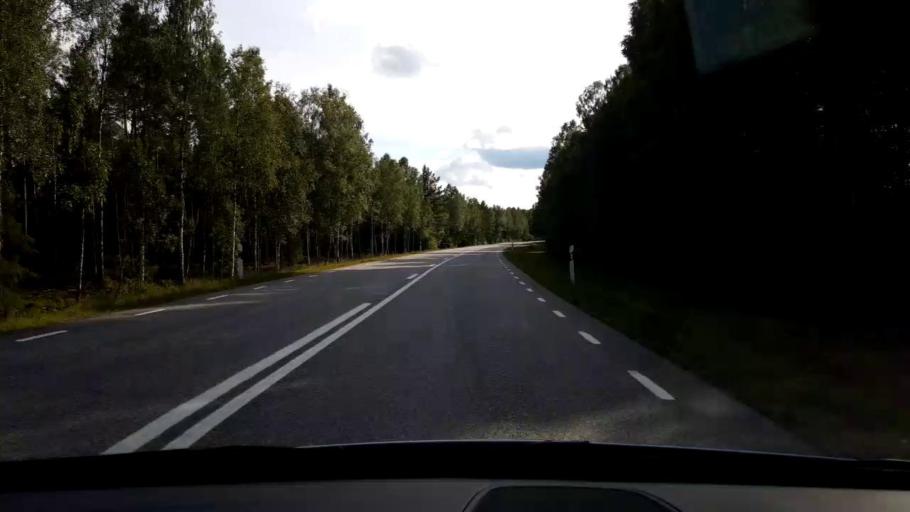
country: SE
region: Joenkoeping
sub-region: Savsjo Kommun
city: Vrigstad
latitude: 57.2942
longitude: 14.3004
